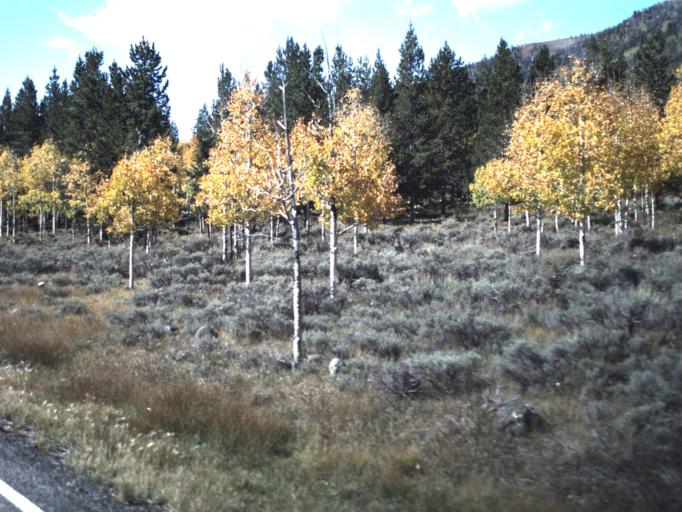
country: US
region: Utah
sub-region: Wayne County
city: Loa
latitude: 38.5555
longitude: -111.7151
